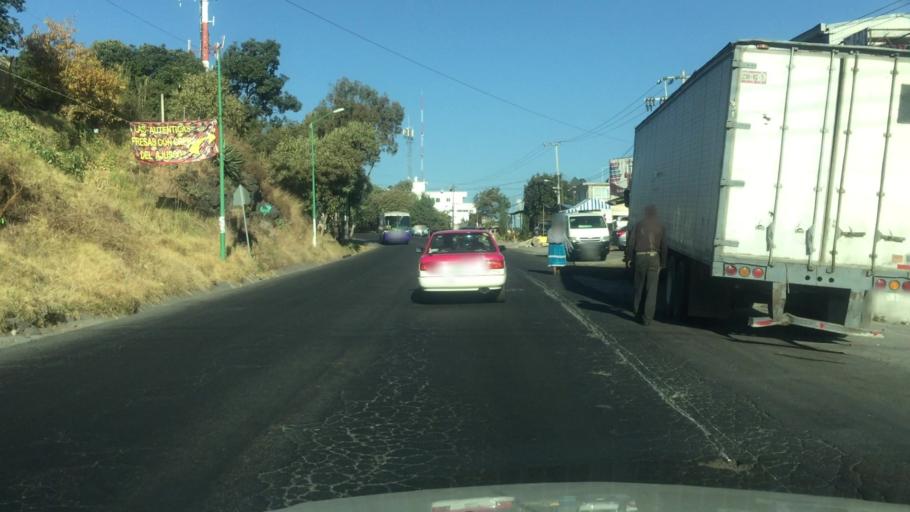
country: MX
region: Mexico City
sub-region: Tlalpan
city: Lomas de Tepemecatl
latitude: 19.2665
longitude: -99.2075
